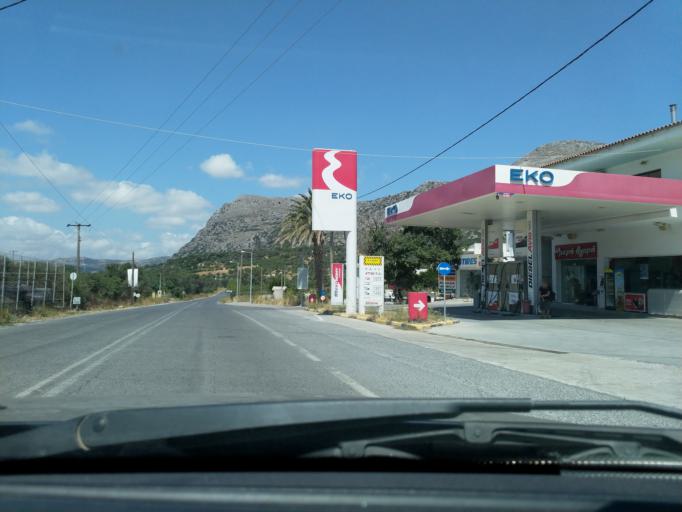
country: GR
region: Crete
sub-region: Nomos Rethymnis
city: Agia Foteini
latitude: 35.1897
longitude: 24.5530
